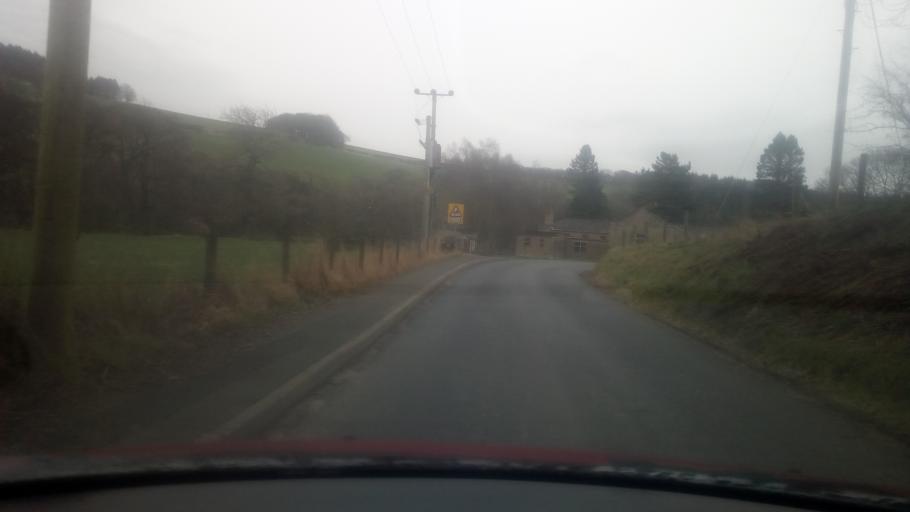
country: GB
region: Scotland
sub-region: The Scottish Borders
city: Hawick
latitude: 55.3934
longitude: -2.6554
